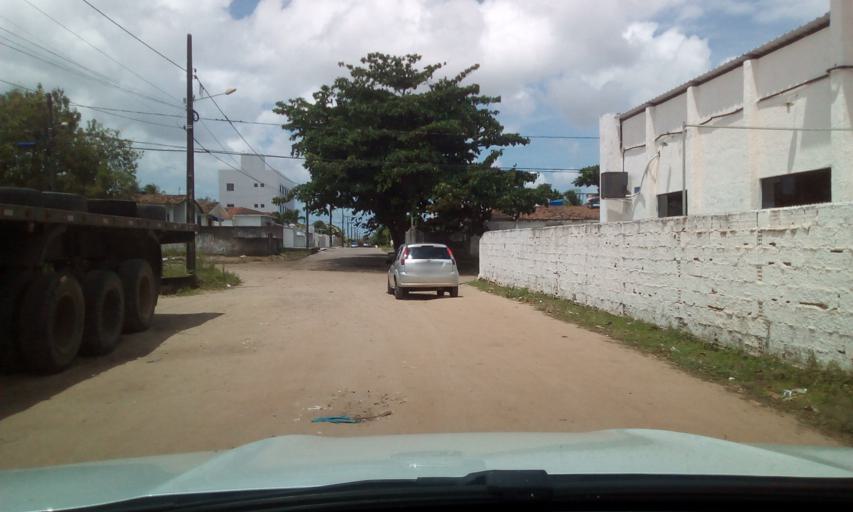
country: BR
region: Paraiba
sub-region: Bayeux
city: Bayeux
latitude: -7.1784
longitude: -34.9173
